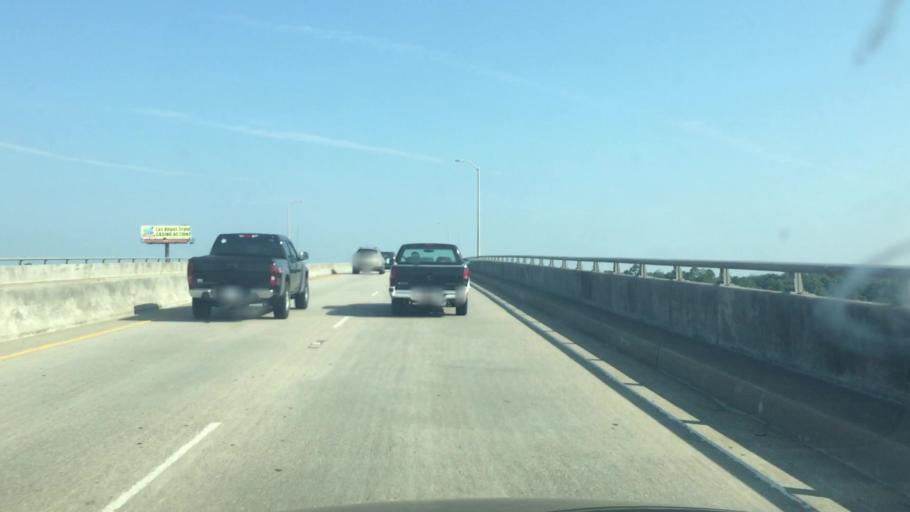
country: US
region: South Carolina
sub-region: Horry County
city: North Myrtle Beach
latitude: 33.8518
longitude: -78.6535
